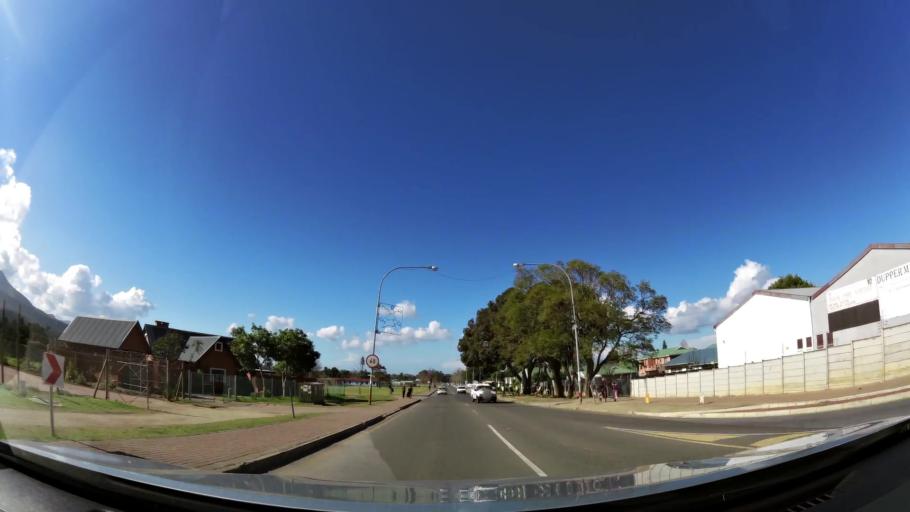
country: ZA
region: Western Cape
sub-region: Eden District Municipality
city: George
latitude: -33.9436
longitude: 22.4129
